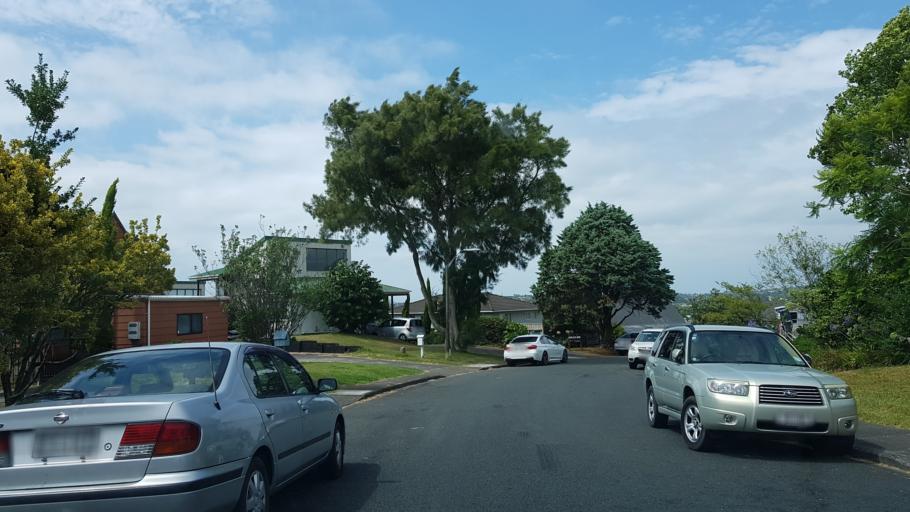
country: NZ
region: Auckland
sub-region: Auckland
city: North Shore
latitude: -36.7674
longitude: 174.7175
